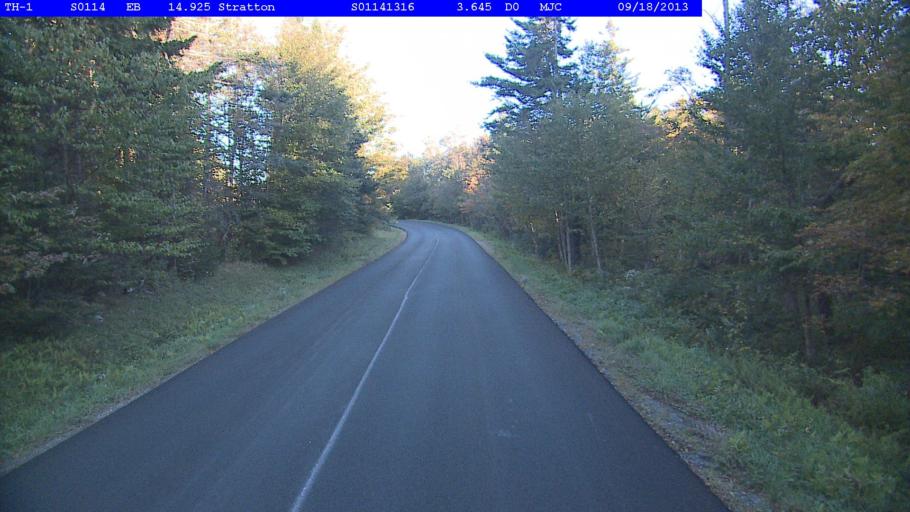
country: US
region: Vermont
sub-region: Bennington County
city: Manchester Center
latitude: 43.0557
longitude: -72.9355
